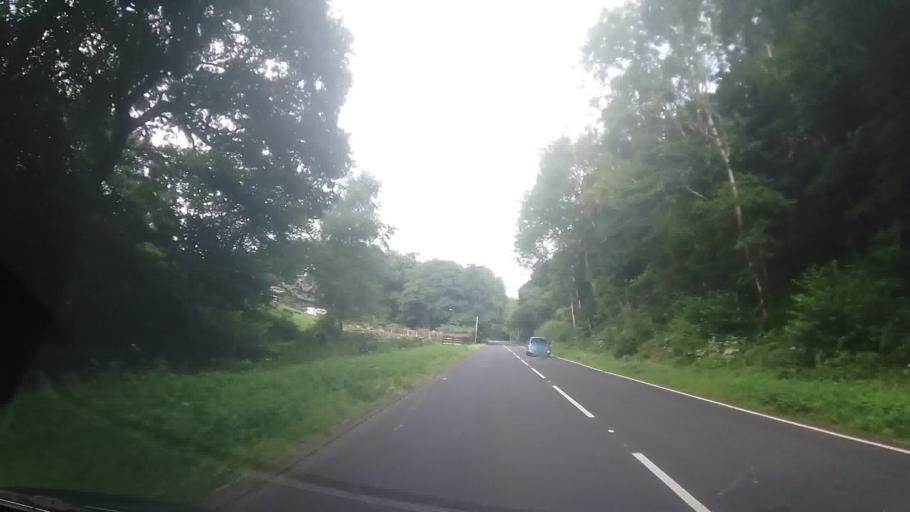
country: GB
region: Wales
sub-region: Gwynedd
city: Barmouth
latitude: 52.7259
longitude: -3.9857
